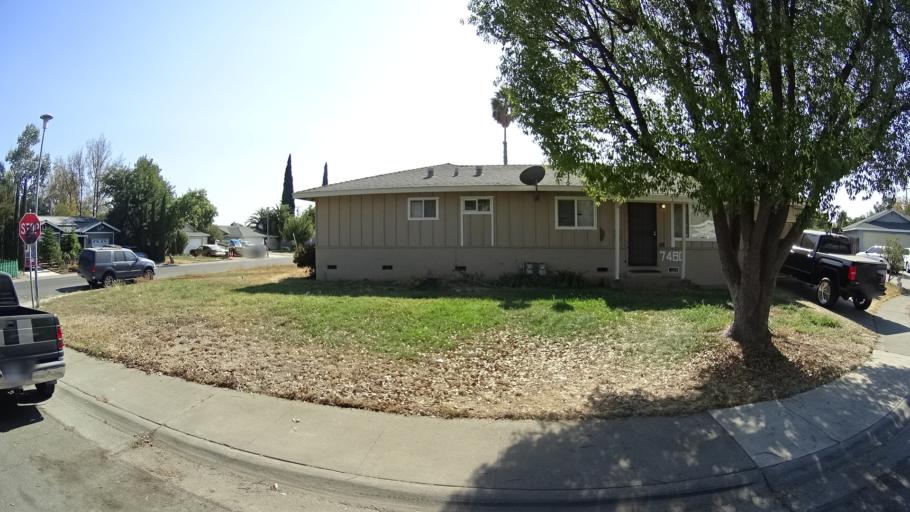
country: US
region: California
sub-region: Sacramento County
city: Parkway
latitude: 38.4862
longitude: -121.4928
